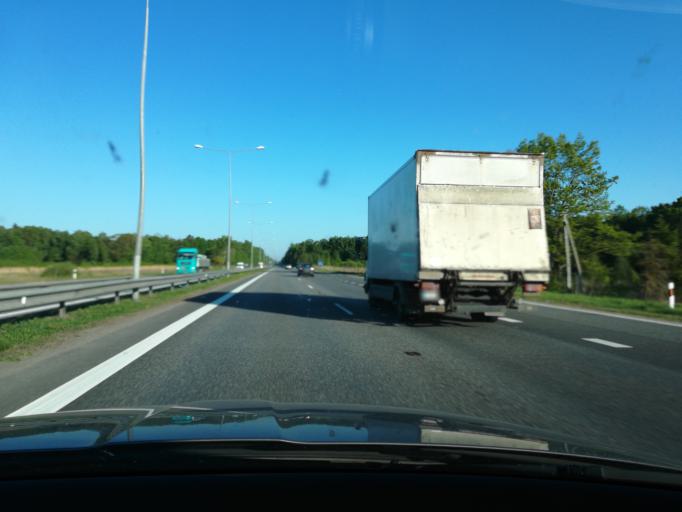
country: LT
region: Kauno apskritis
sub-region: Kauno rajonas
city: Karmelava
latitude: 54.8973
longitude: 24.1458
